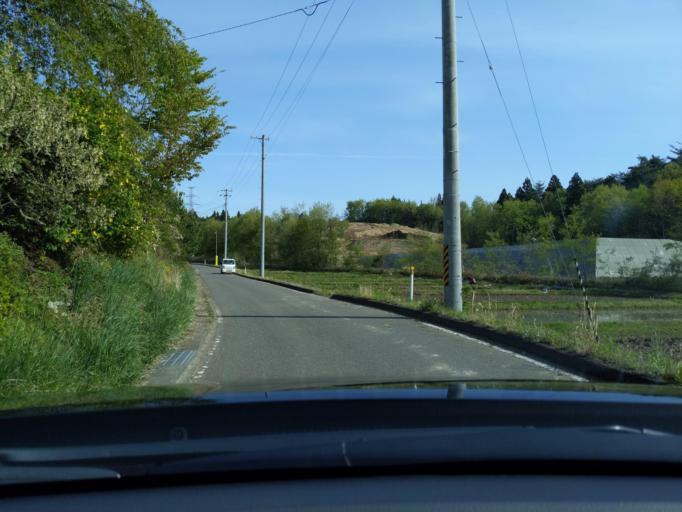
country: JP
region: Fukushima
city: Sukagawa
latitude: 37.3129
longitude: 140.4239
